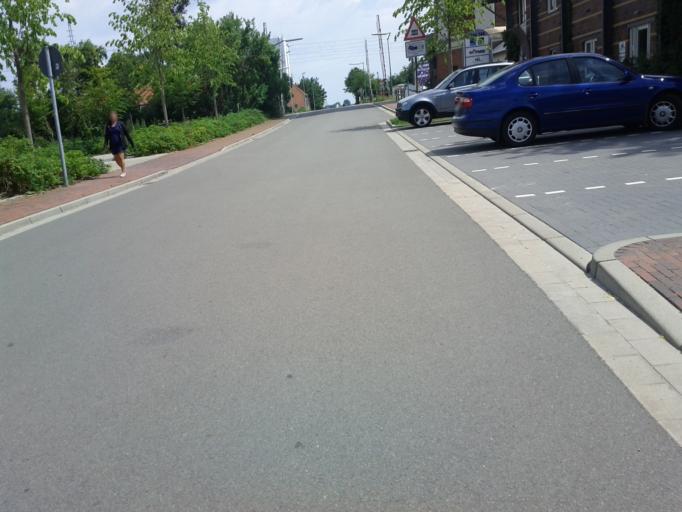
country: DE
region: Lower Saxony
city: Oldenburg
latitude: 53.1406
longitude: 8.2321
